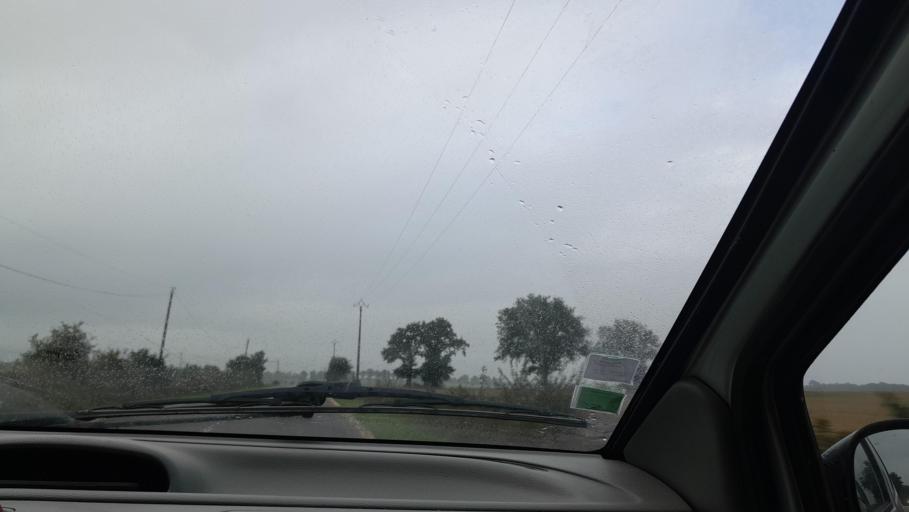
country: FR
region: Pays de la Loire
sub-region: Departement de la Mayenne
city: Congrier
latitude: 47.8151
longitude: -1.1471
